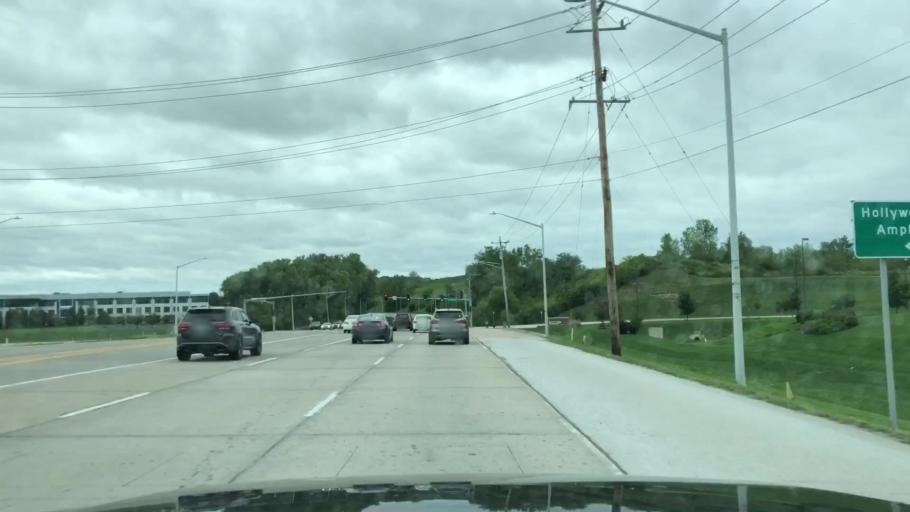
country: US
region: Missouri
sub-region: Saint Charles County
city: Saint Charles
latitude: 38.7432
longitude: -90.4683
